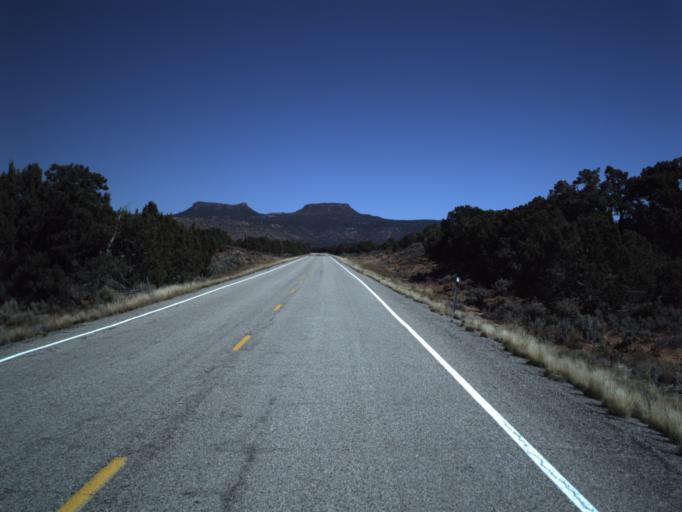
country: US
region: Utah
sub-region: San Juan County
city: Blanding
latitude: 37.5492
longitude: -109.9413
